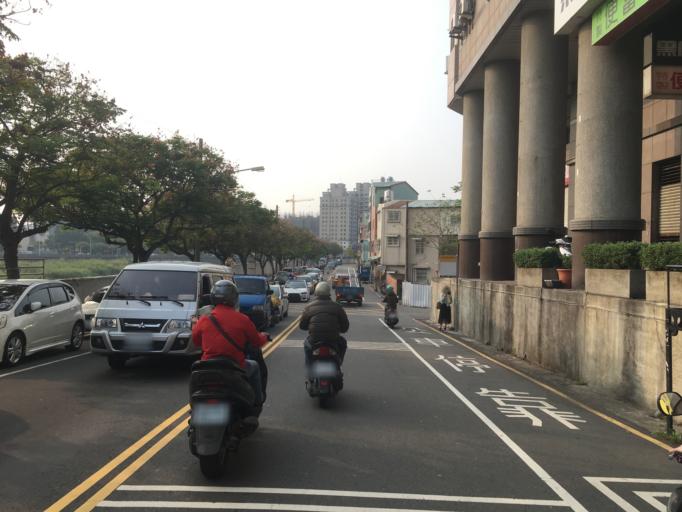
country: TW
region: Taiwan
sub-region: Taichung City
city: Taichung
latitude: 24.1692
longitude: 120.7049
